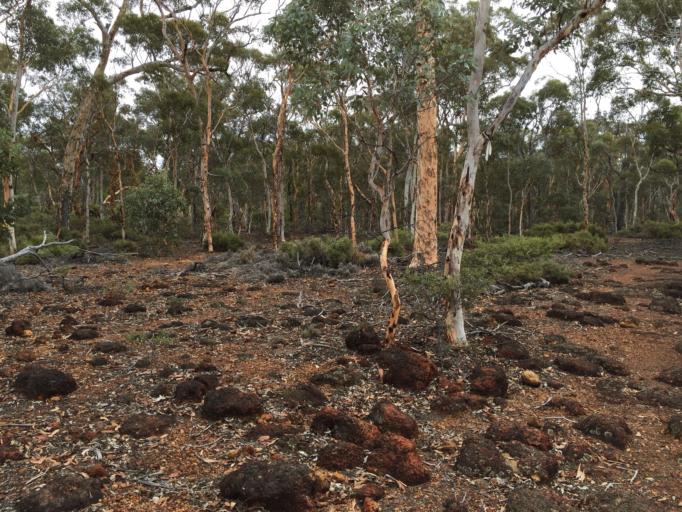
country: AU
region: Western Australia
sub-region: Narrogin
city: Narrogin
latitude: -32.7968
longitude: 116.9428
